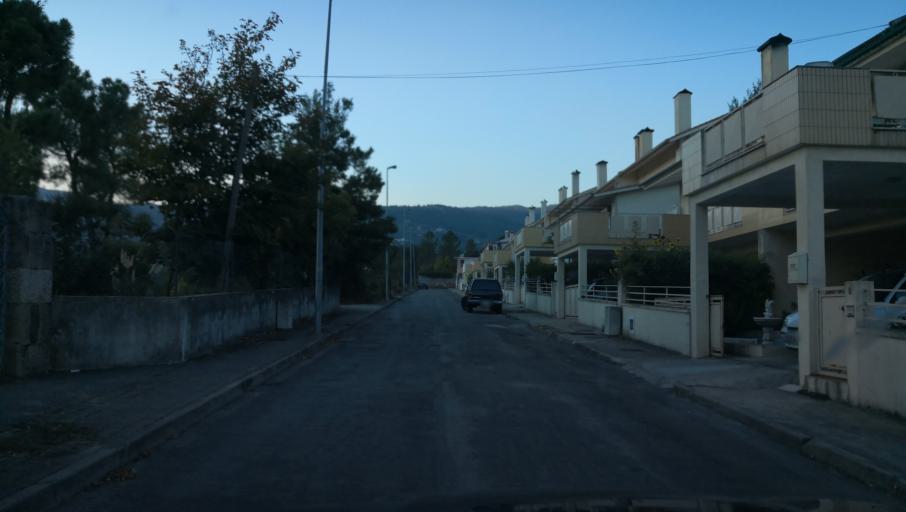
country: PT
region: Vila Real
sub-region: Vila Real
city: Vila Real
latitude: 41.3058
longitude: -7.7671
